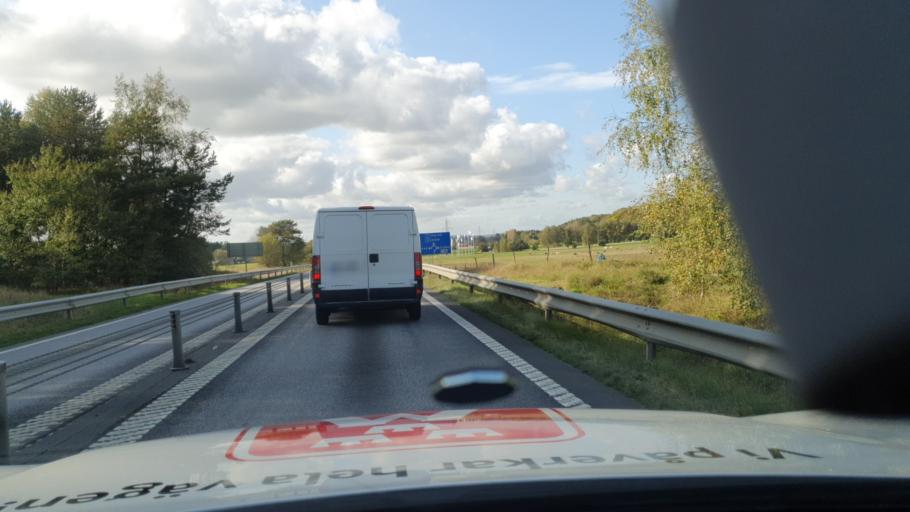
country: SE
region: Skane
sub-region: Sjobo Kommun
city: Sjoebo
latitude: 55.6227
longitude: 13.7124
